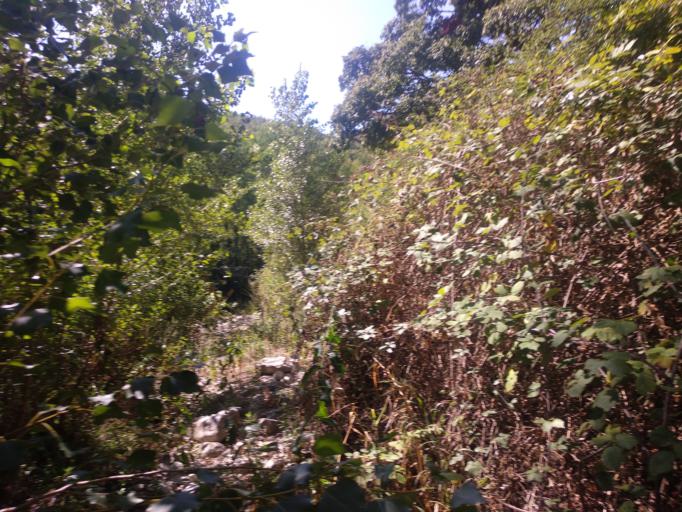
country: FR
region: Rhone-Alpes
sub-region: Departement de l'Ardeche
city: Sarras
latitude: 45.1924
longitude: 4.7876
